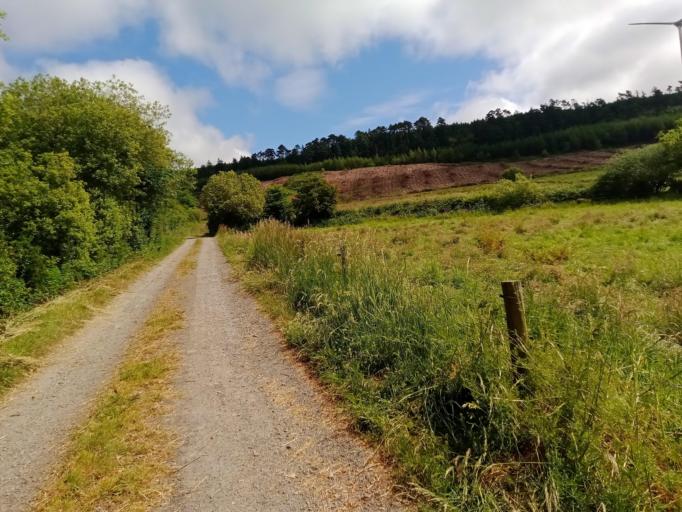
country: IE
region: Leinster
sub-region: Kilkenny
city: Ballyragget
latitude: 52.7854
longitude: -7.4475
